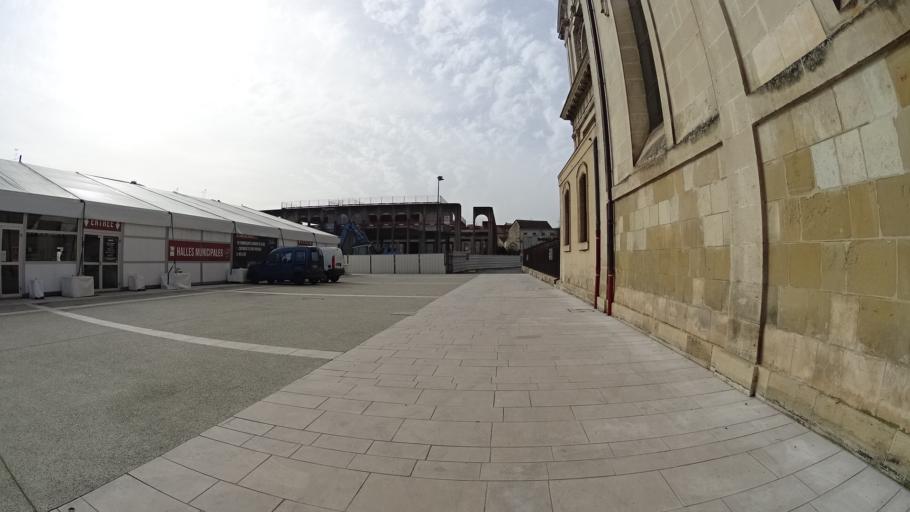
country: FR
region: Aquitaine
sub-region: Departement des Landes
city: Dax
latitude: 43.7082
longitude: -1.0526
